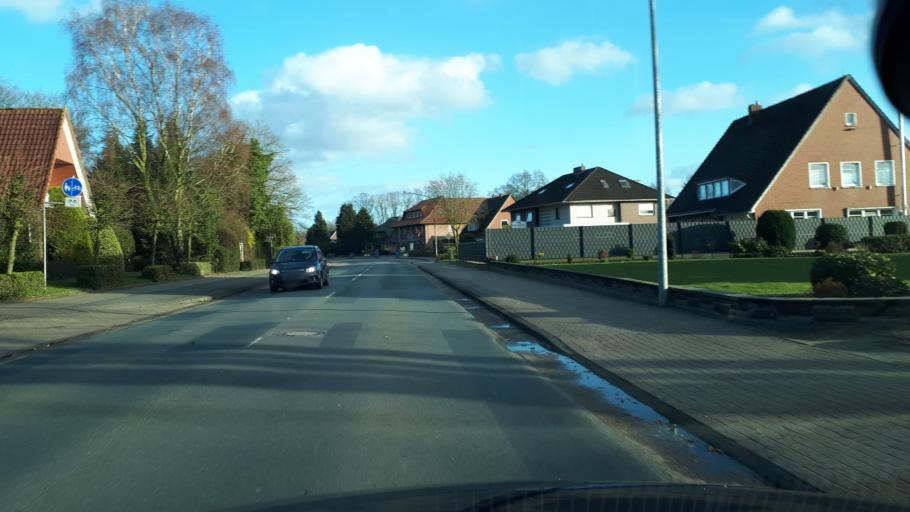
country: DE
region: Lower Saxony
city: Molbergen
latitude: 52.8605
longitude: 7.9143
